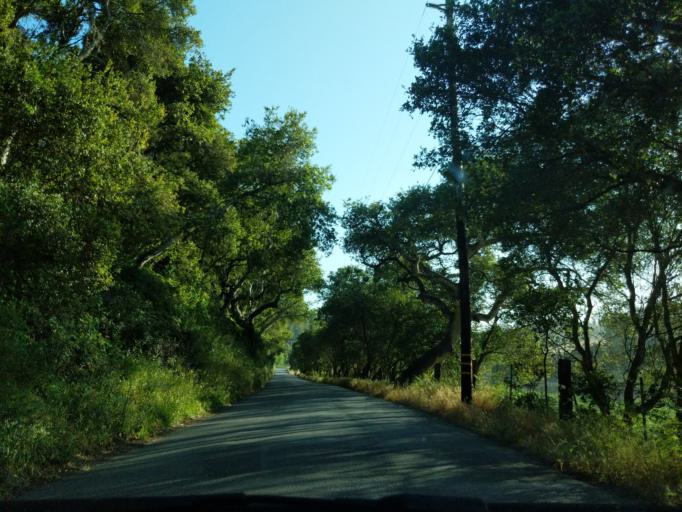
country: US
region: California
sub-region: Monterey County
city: Las Lomas
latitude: 36.8864
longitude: -121.7245
